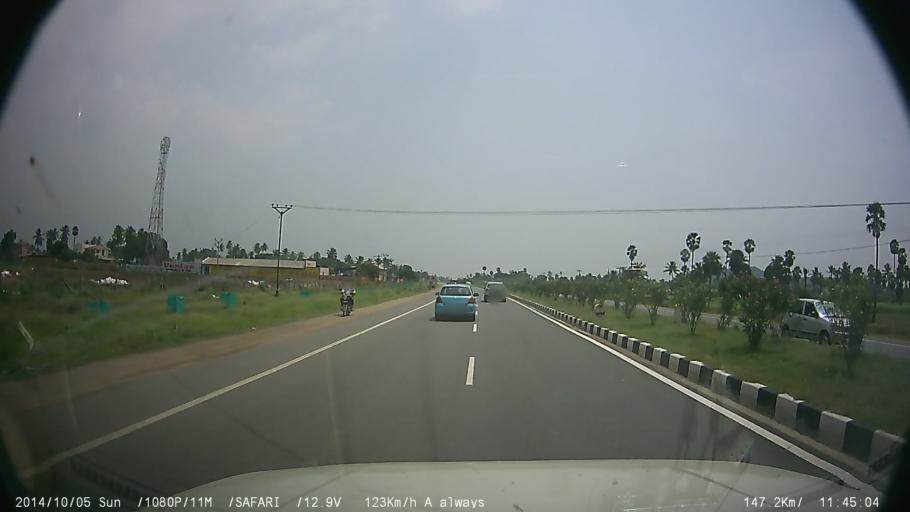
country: IN
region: Tamil Nadu
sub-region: Salem
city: Attur
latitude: 11.5923
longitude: 78.6474
